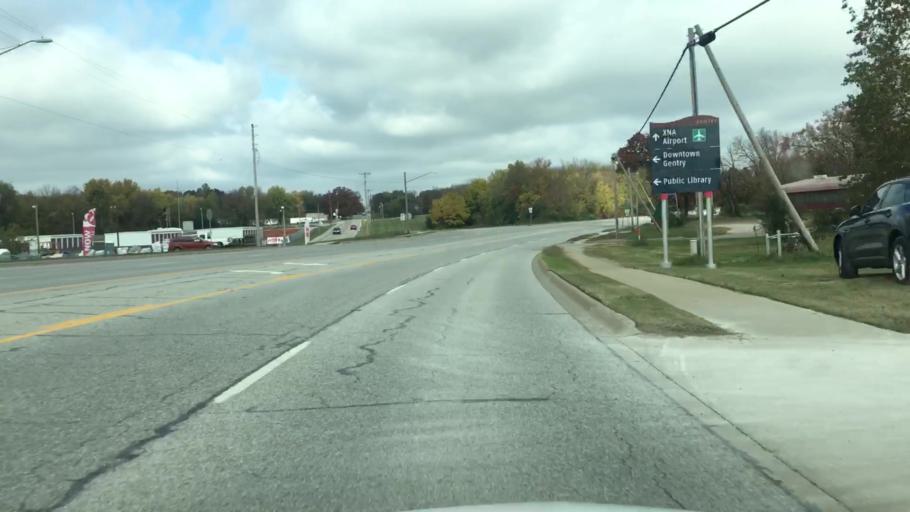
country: US
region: Arkansas
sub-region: Benton County
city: Gentry
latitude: 36.2589
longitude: -94.4850
